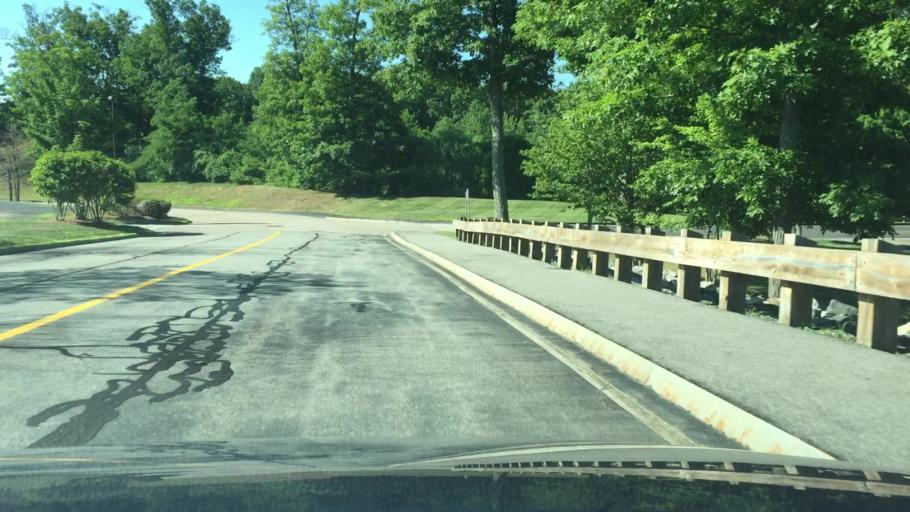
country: US
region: Massachusetts
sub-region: Middlesex County
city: Marlborough
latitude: 42.3237
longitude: -71.5859
